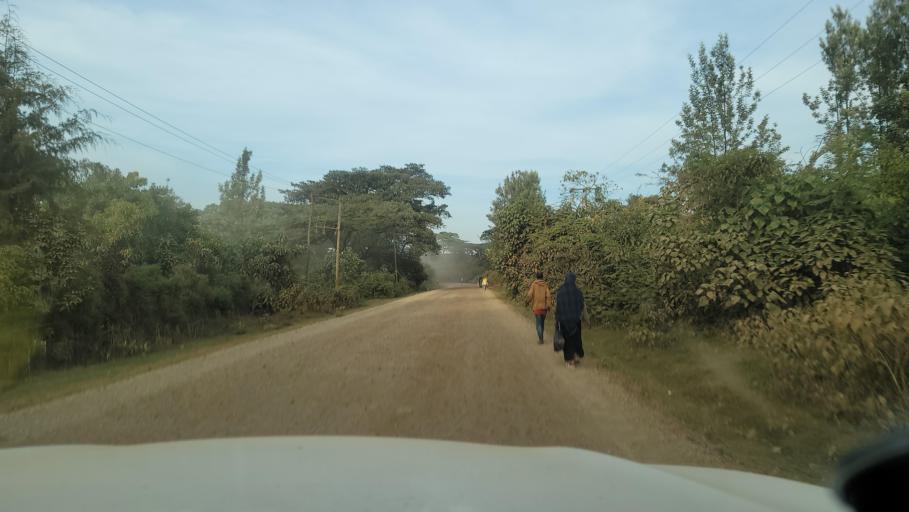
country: ET
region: Oromiya
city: Agaro
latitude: 7.8436
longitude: 36.5627
